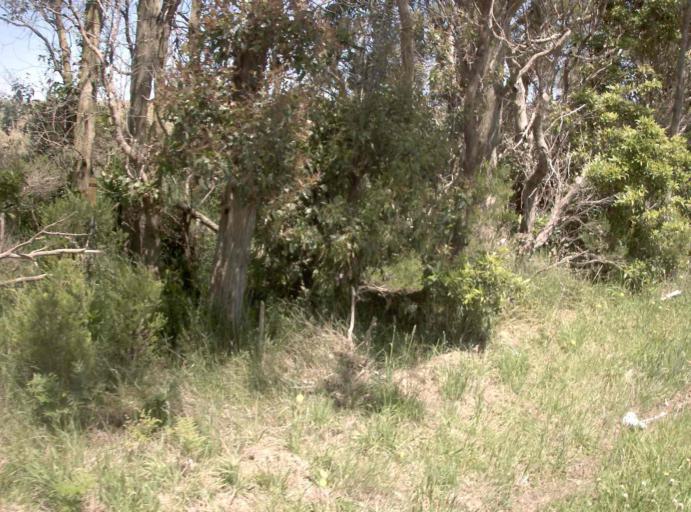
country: AU
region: Victoria
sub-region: Bass Coast
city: North Wonthaggi
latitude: -38.7497
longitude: 146.0749
